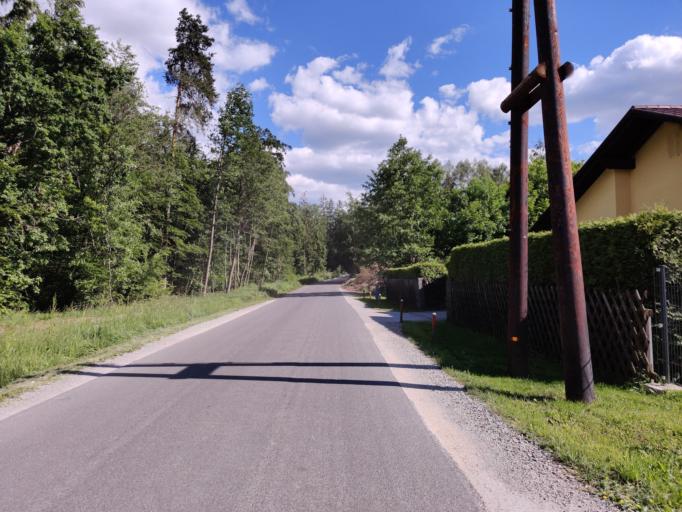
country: AT
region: Styria
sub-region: Politischer Bezirk Graz-Umgebung
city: Thal
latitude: 47.0453
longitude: 15.3634
